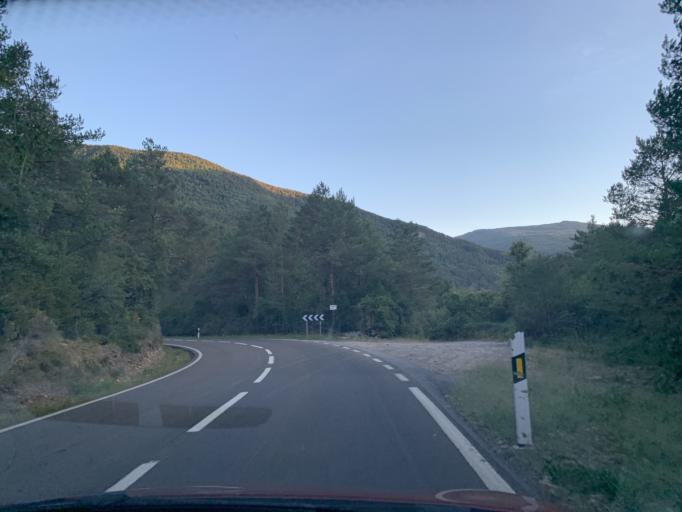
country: ES
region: Aragon
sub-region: Provincia de Huesca
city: Broto
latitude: 42.5550
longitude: -0.1216
